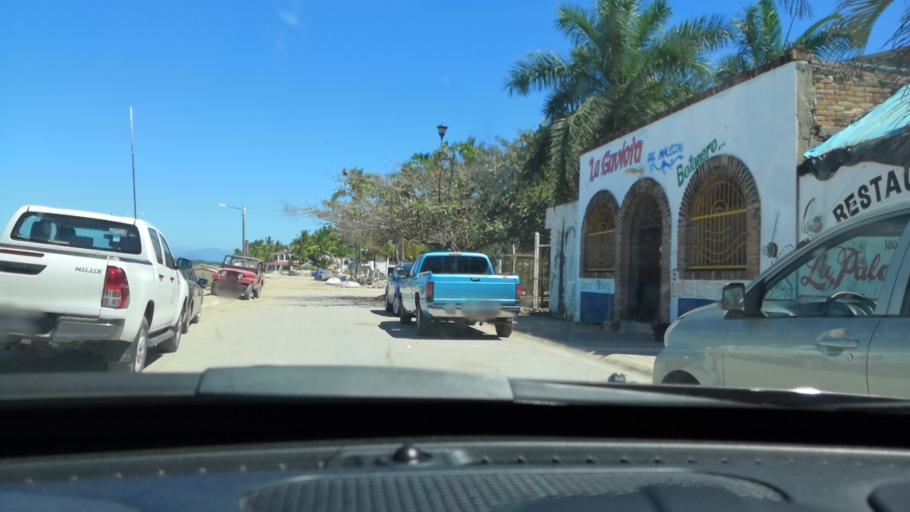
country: MX
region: Nayarit
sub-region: Compostela
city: Colonia Paraiso Escondido
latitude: 21.0423
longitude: -105.2502
